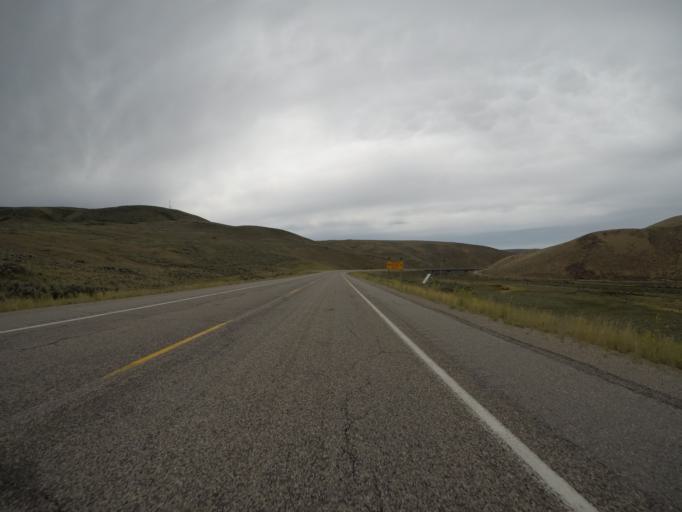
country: US
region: Wyoming
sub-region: Lincoln County
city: Kemmerer
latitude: 41.8175
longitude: -110.8014
